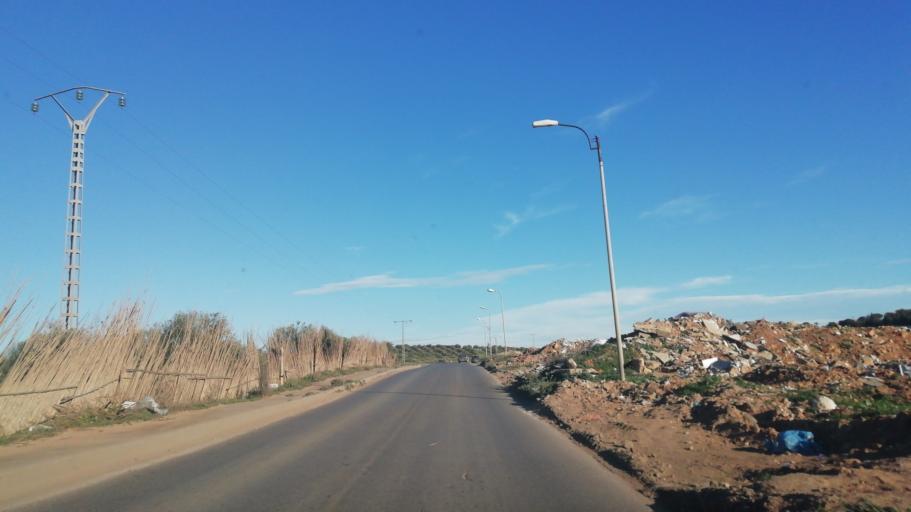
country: DZ
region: Oran
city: Sidi ech Chahmi
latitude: 35.6823
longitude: -0.4941
